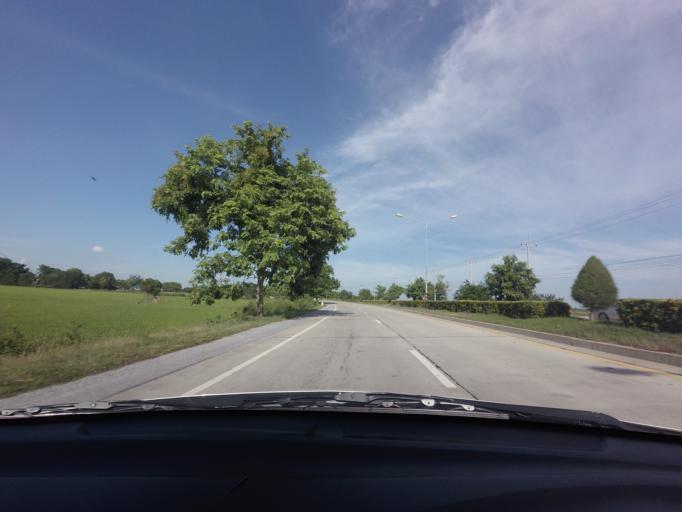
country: TH
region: Suphan Buri
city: Suphan Buri
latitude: 14.4564
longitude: 100.0590
